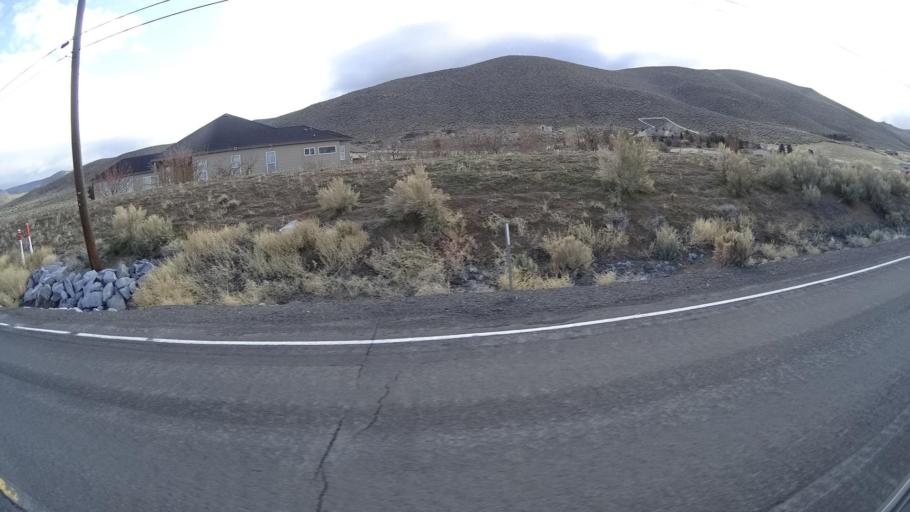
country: US
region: Nevada
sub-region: Carson City
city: Carson City
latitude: 39.2686
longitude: -119.7566
